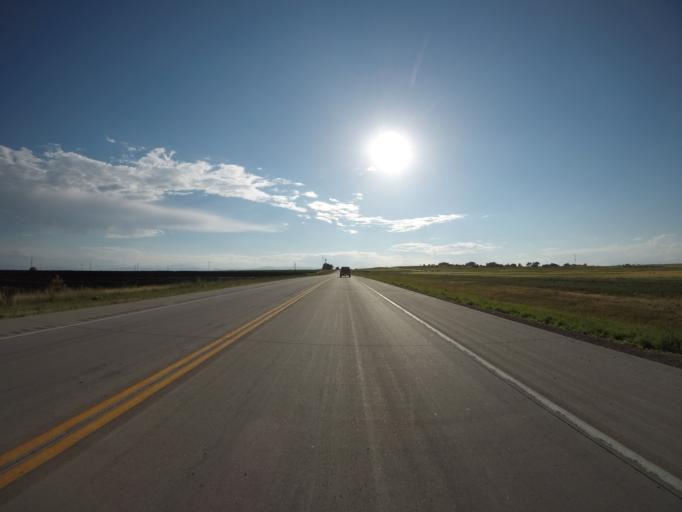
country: US
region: Colorado
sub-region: Weld County
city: Severance
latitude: 40.5815
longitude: -104.8952
